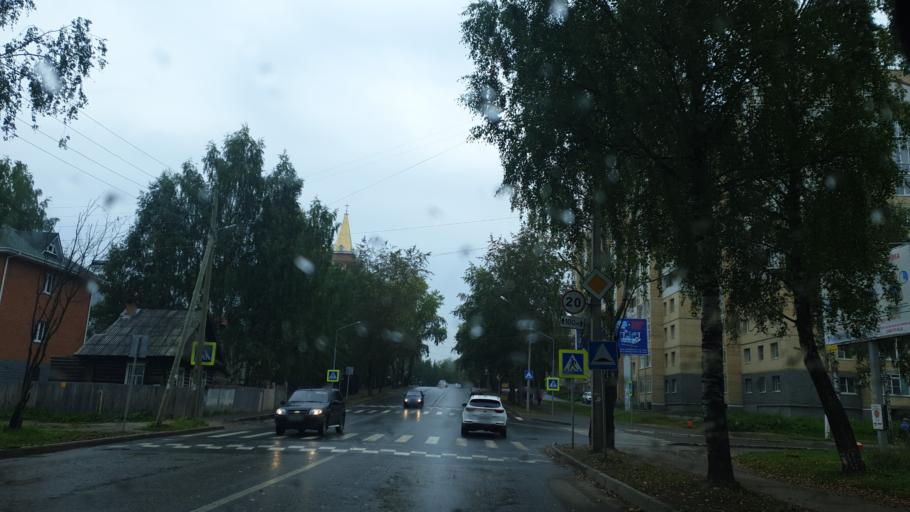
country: RU
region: Komi Republic
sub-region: Syktyvdinskiy Rayon
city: Syktyvkar
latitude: 61.6592
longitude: 50.8258
